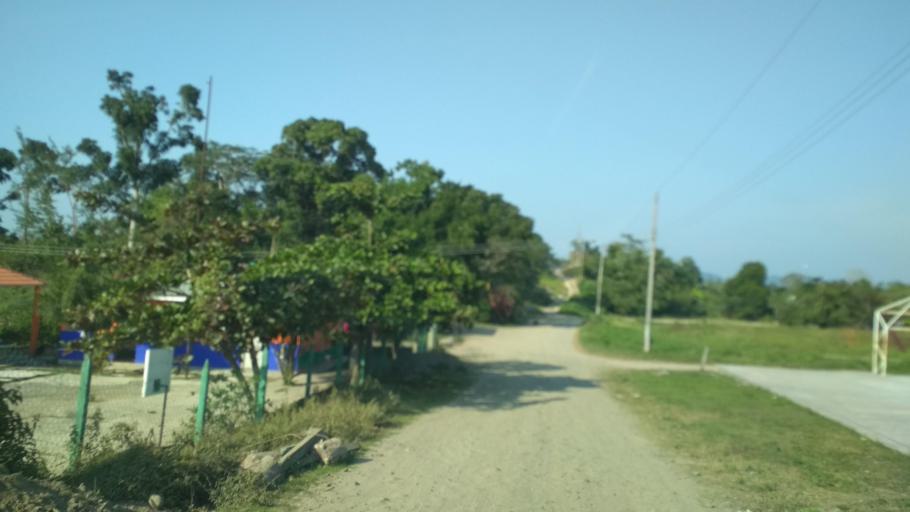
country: MX
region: Puebla
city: San Jose Acateno
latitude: 20.2176
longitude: -97.2637
